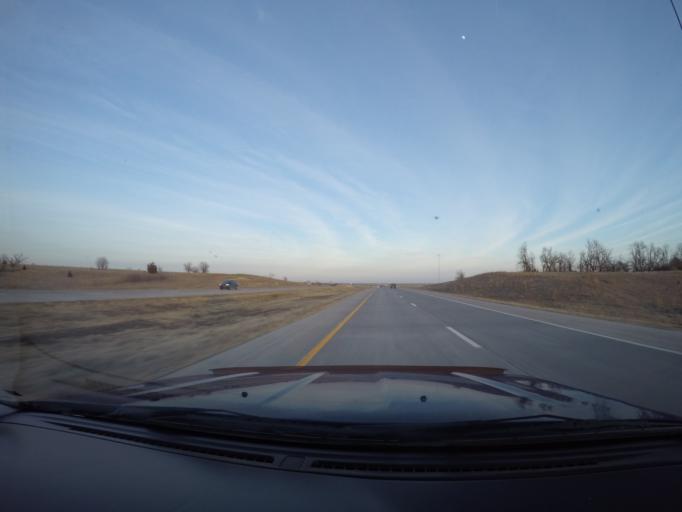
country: US
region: Kansas
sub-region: Dickinson County
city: Solomon
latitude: 38.9070
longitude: -97.4935
